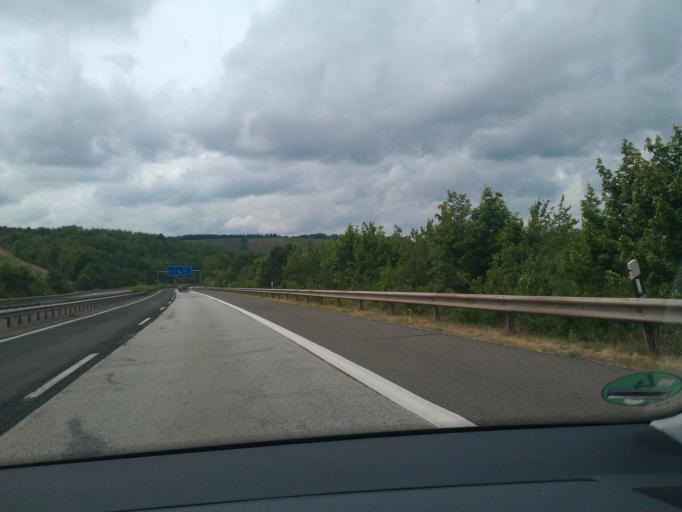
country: DE
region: Rheinland-Pfalz
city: Longuich
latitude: 49.7987
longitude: 6.7703
